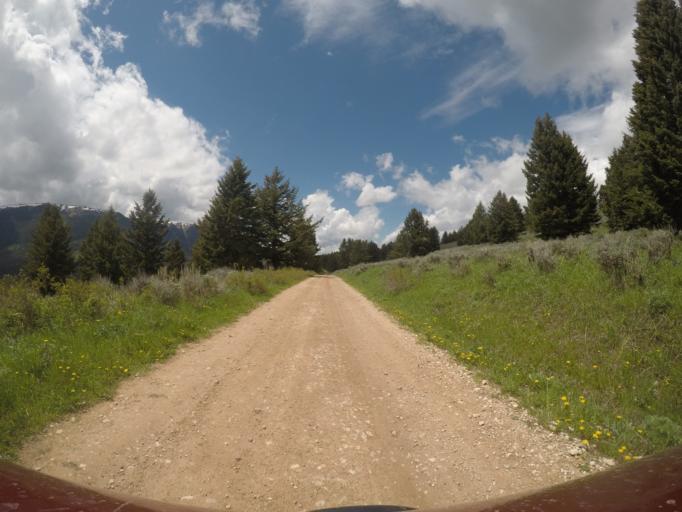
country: US
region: Wyoming
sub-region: Big Horn County
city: Lovell
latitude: 45.1698
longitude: -108.4271
